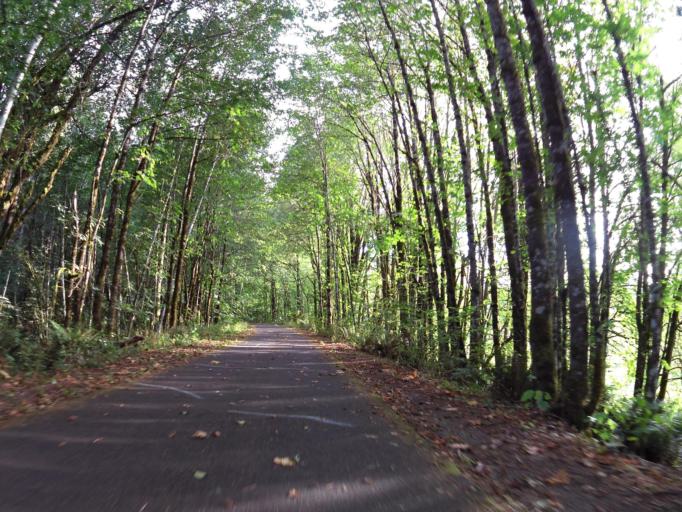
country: US
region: Washington
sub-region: Thurston County
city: Tenino
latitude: 46.9348
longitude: -122.8239
